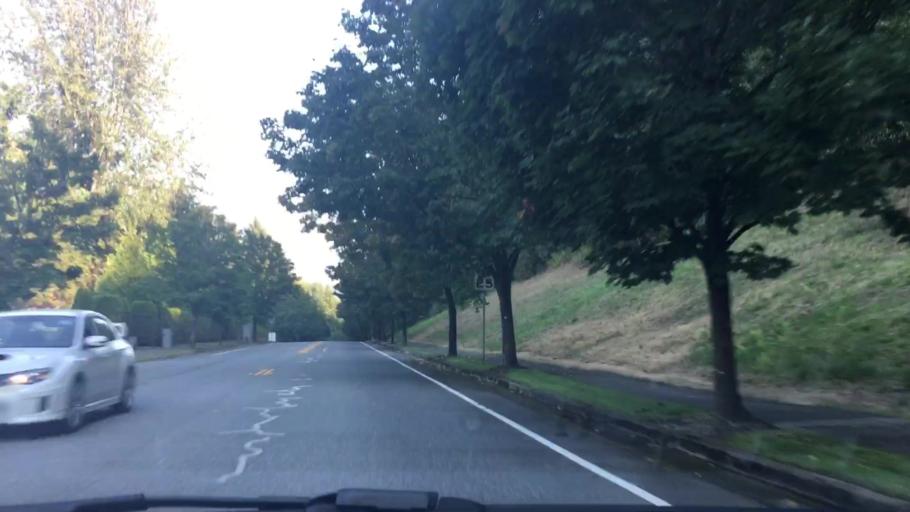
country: US
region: Washington
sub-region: King County
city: West Lake Sammamish
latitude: 47.5584
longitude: -122.0920
